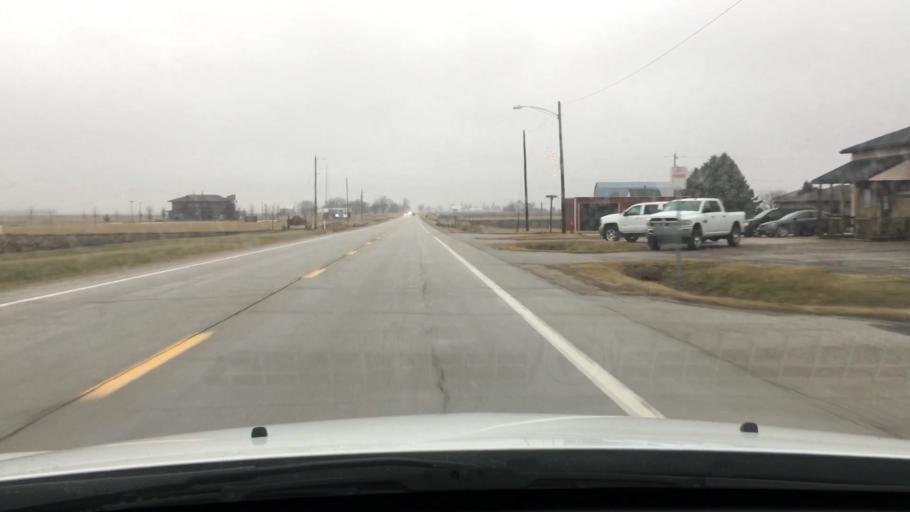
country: US
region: Illinois
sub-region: Livingston County
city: Flanagan
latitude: 40.8710
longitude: -88.8619
